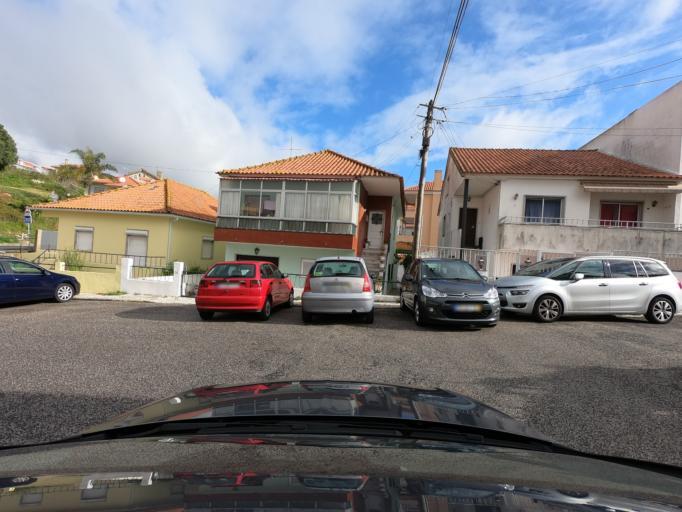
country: PT
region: Lisbon
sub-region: Oeiras
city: Porto Salvo
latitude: 38.7240
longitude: -9.3096
